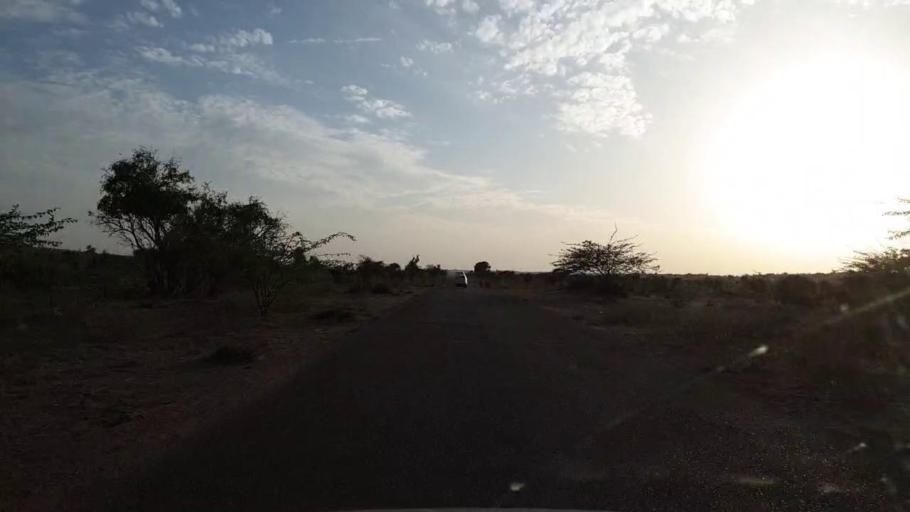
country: PK
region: Sindh
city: Nabisar
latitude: 25.0807
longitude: 69.9830
